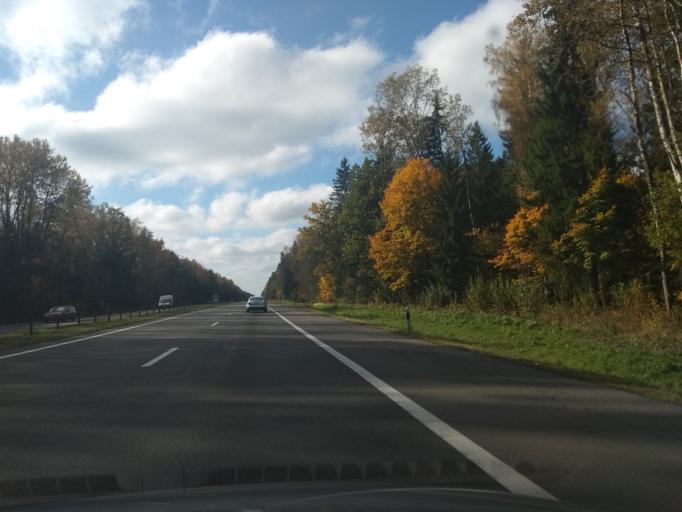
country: BY
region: Minsk
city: Enyerhyetykaw
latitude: 53.5815
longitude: 27.0236
